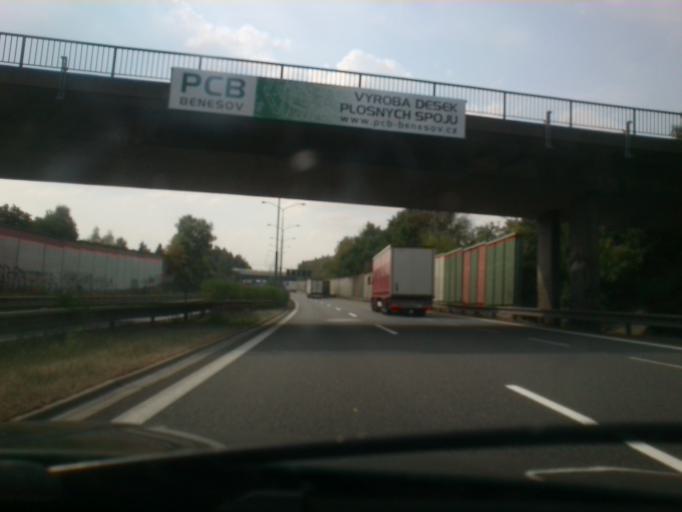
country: CZ
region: Central Bohemia
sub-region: Okres Praha-Vychod
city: Mnichovice
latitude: 49.9106
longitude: 14.7247
